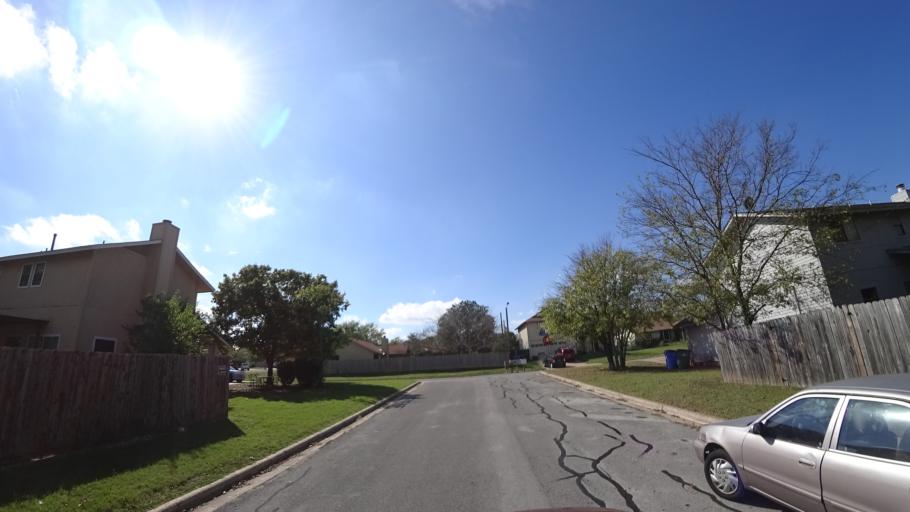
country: US
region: Texas
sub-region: Travis County
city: Windemere
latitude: 30.4578
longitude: -97.6463
